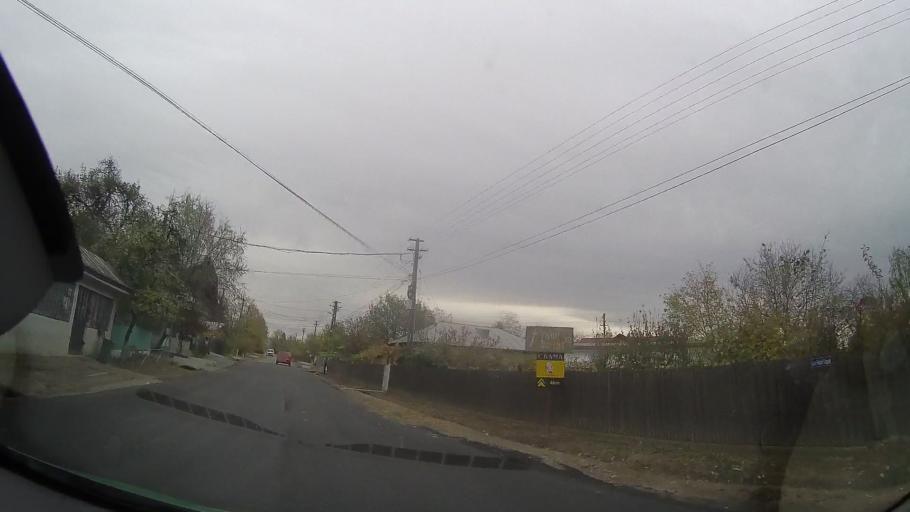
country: RO
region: Prahova
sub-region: Comuna Fantanele
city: Fantanele
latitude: 45.0095
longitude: 26.3779
